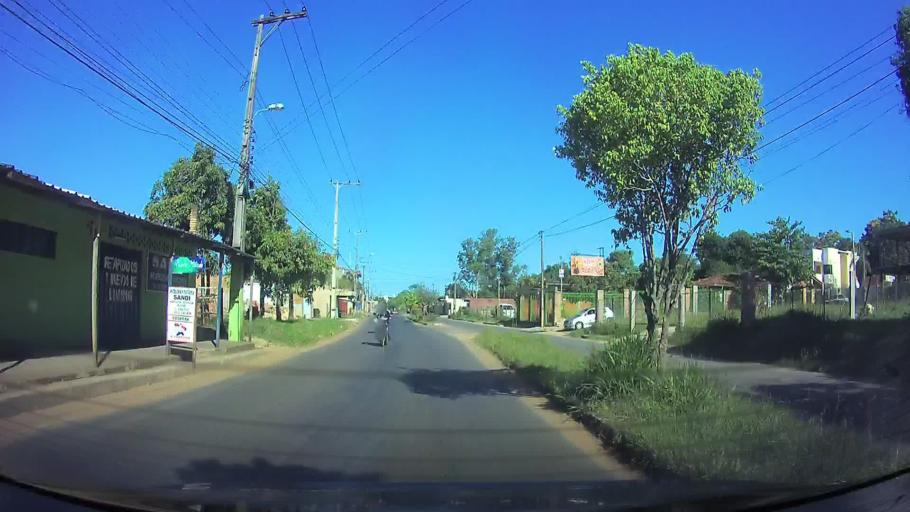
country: PY
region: Central
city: San Lorenzo
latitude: -25.2989
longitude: -57.5076
